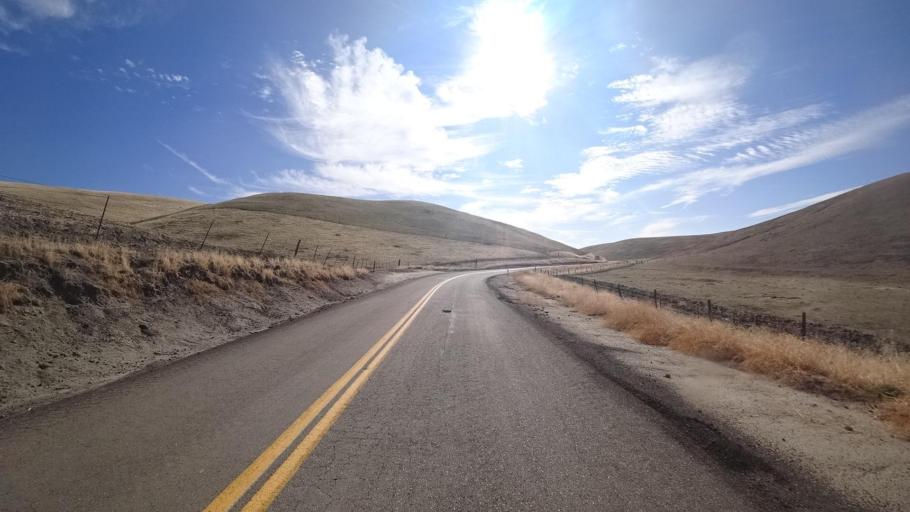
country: US
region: California
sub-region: Kern County
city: Oildale
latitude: 35.6181
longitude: -118.9421
